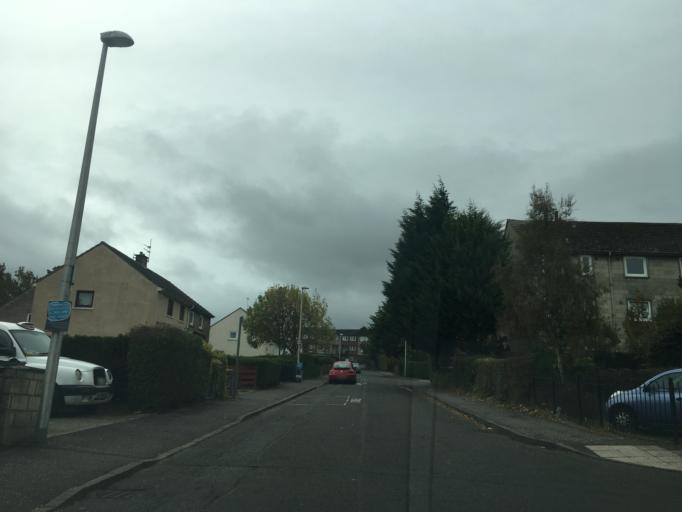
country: GB
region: Scotland
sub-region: Edinburgh
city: Colinton
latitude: 55.9073
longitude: -3.2225
